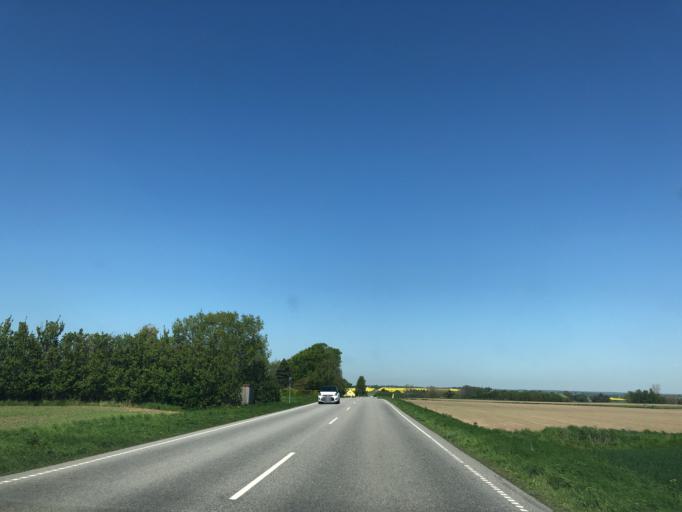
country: DK
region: Zealand
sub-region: Slagelse Kommune
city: Skaelskor
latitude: 55.3084
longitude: 11.2921
